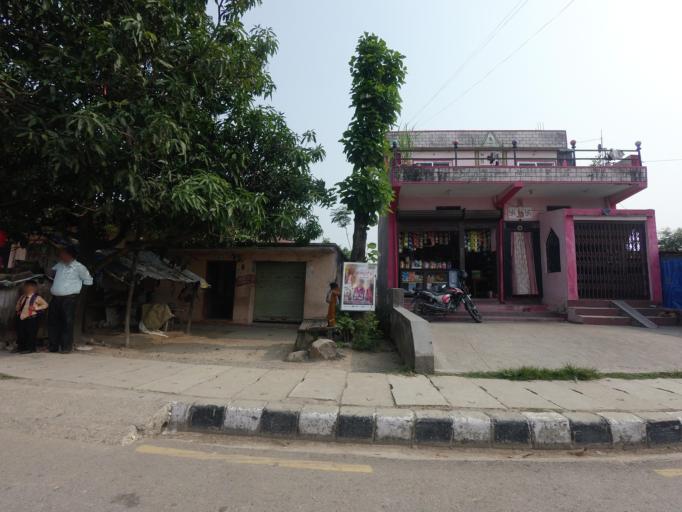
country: NP
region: Western Region
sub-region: Lumbini Zone
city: Bhairahawa
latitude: 27.5178
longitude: 83.4622
